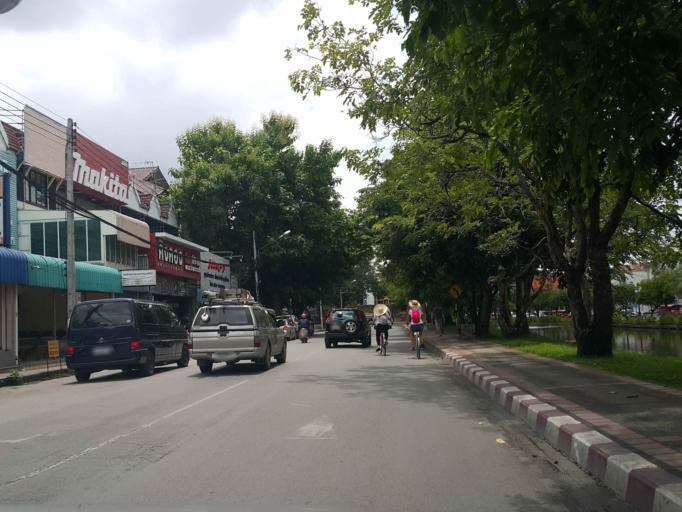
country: TH
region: Chiang Mai
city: Chiang Mai
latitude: 18.7813
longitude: 98.9911
